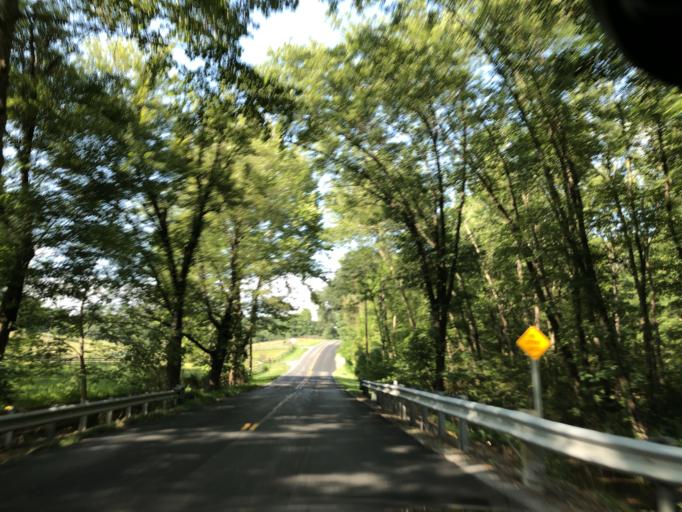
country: US
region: Maryland
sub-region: Frederick County
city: Linganore
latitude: 39.4385
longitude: -77.1795
